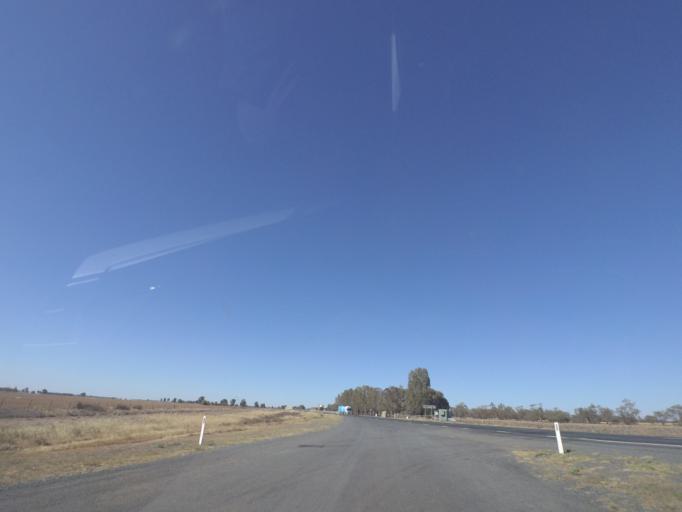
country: AU
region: New South Wales
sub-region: Bland
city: West Wyalong
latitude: -33.7655
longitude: 147.5181
